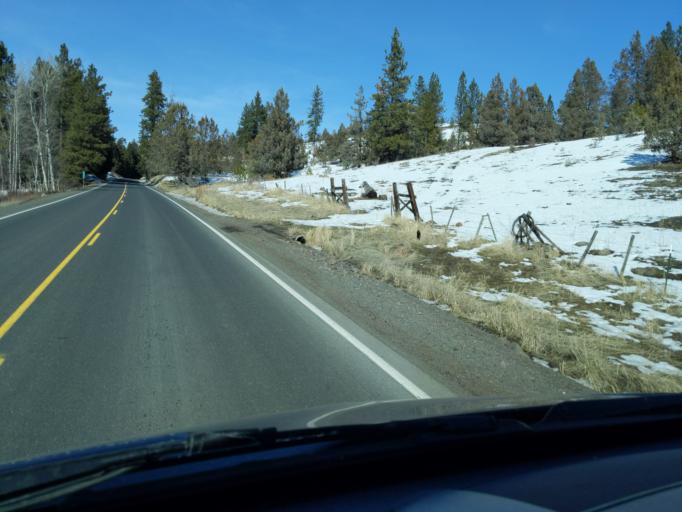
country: US
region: Oregon
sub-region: Grant County
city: John Day
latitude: 44.8809
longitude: -119.0147
